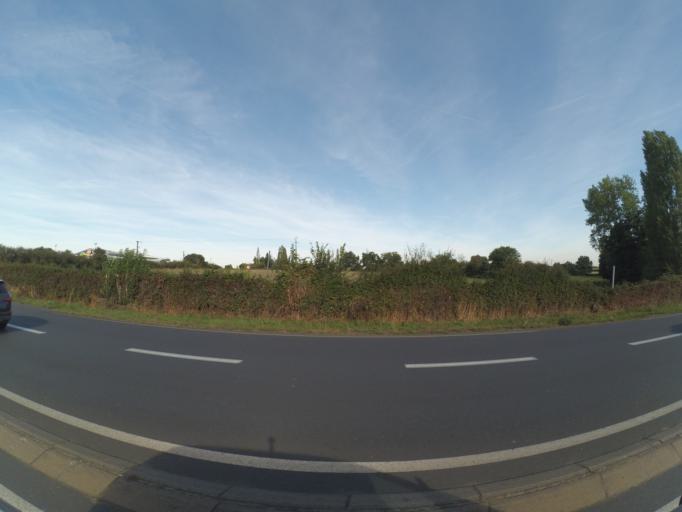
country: FR
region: Pays de la Loire
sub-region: Departement de Maine-et-Loire
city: Mazieres-en-Mauges
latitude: 47.0790
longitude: -0.8325
